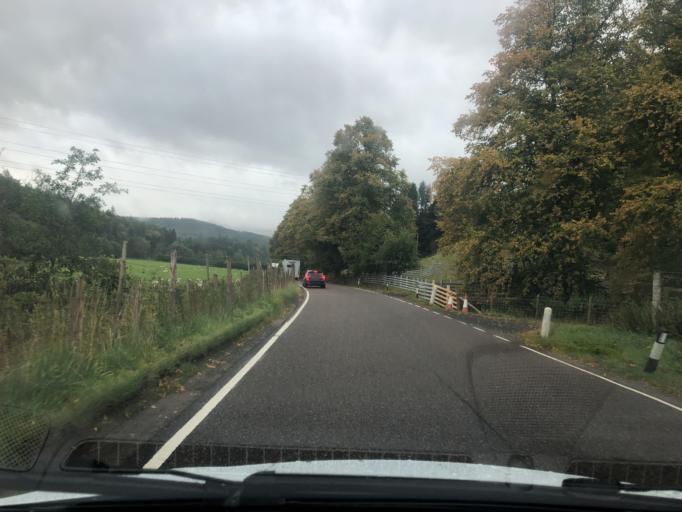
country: GB
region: Scotland
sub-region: Highland
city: Kingussie
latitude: 56.9809
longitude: -4.3738
